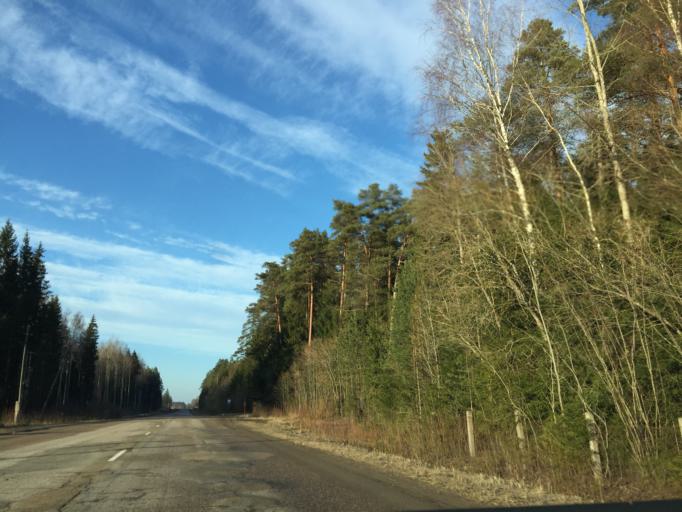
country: LV
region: Lecava
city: Iecava
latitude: 56.7190
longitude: 24.1115
